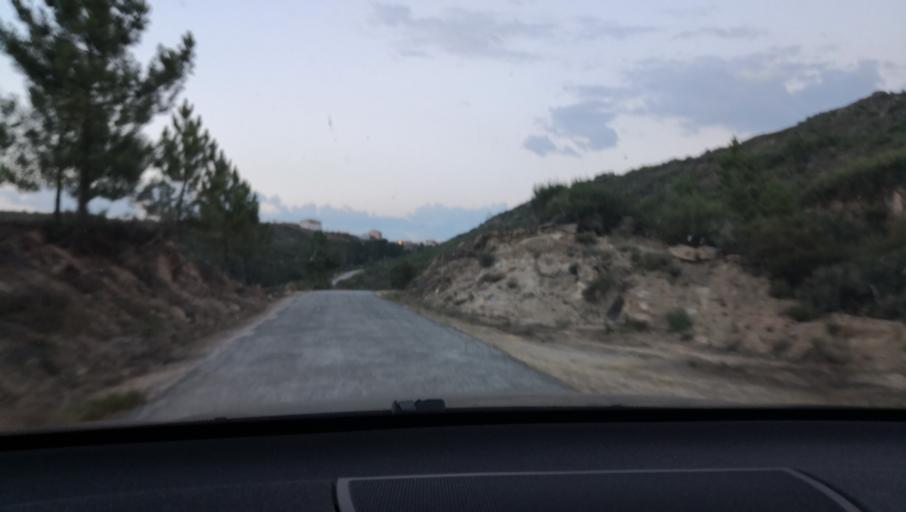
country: PT
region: Vila Real
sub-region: Sabrosa
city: Sabrosa
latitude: 41.2857
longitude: -7.6220
